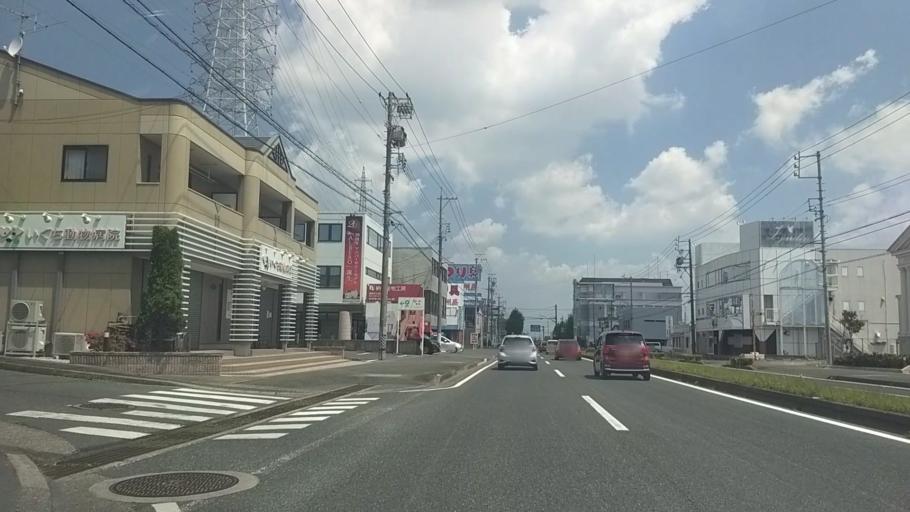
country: JP
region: Shizuoka
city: Hamamatsu
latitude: 34.7402
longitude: 137.7379
